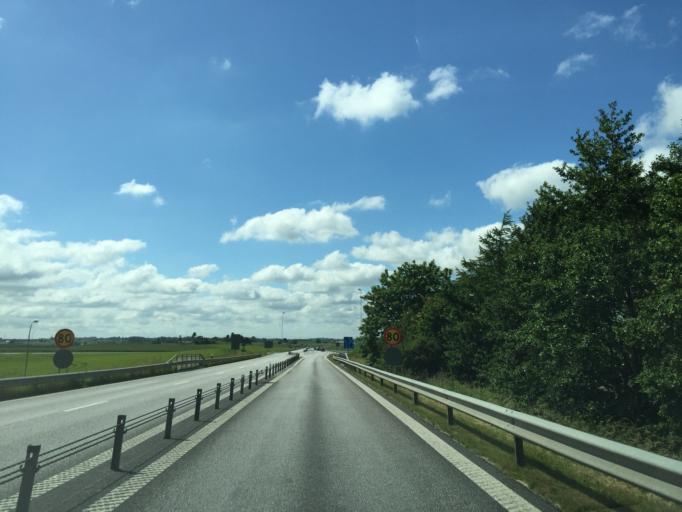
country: SE
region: Skane
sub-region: Skurups Kommun
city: Rydsgard
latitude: 55.4827
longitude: 13.5967
